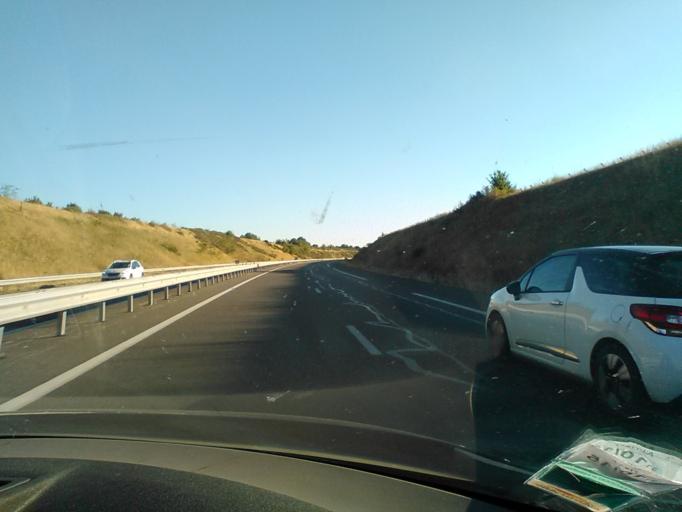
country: FR
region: Rhone-Alpes
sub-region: Departement de l'Isere
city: Satolas-et-Bonce
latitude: 45.7048
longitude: 5.0991
